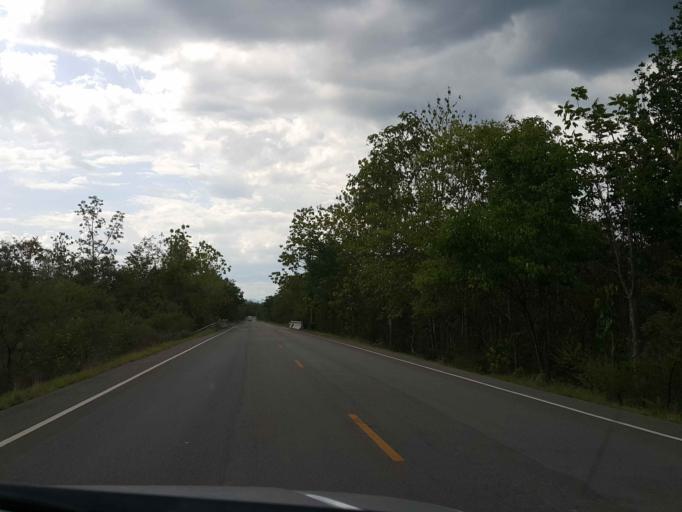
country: TH
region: Sukhothai
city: Thung Saliam
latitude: 17.3723
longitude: 99.4045
